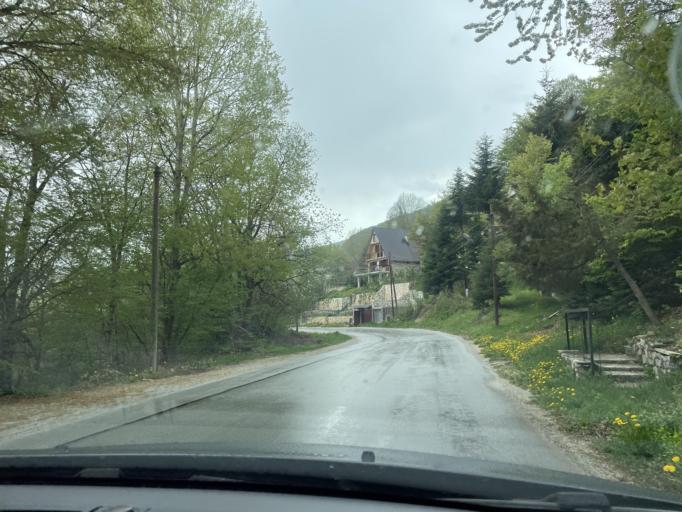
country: MK
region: Gostivar
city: Vrutok
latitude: 41.6836
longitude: 20.7397
